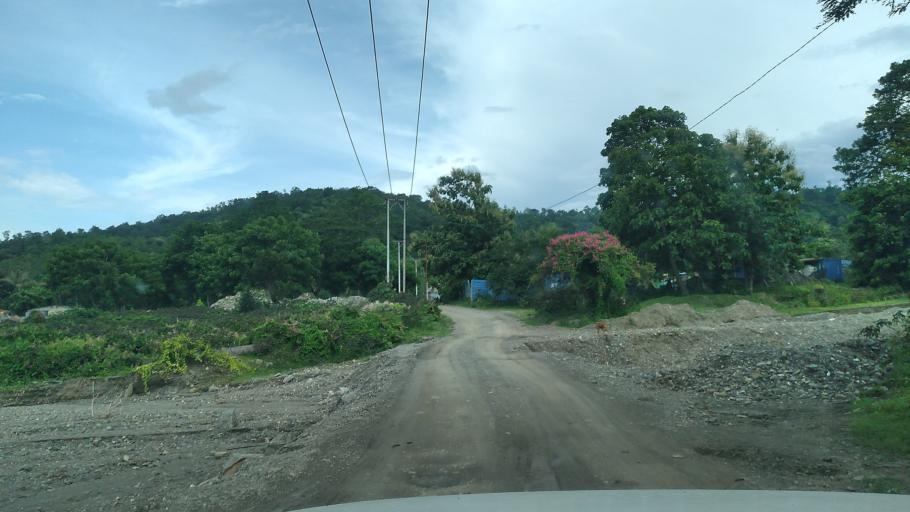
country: TL
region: Dili
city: Dili
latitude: -8.5983
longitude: 125.4807
